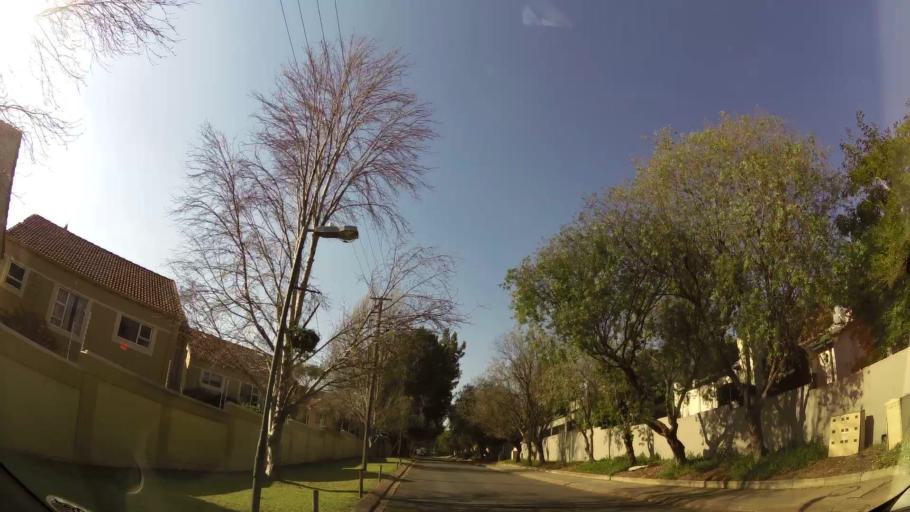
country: ZA
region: Gauteng
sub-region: City of Johannesburg Metropolitan Municipality
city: Diepsloot
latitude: -26.0682
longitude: 28.0119
